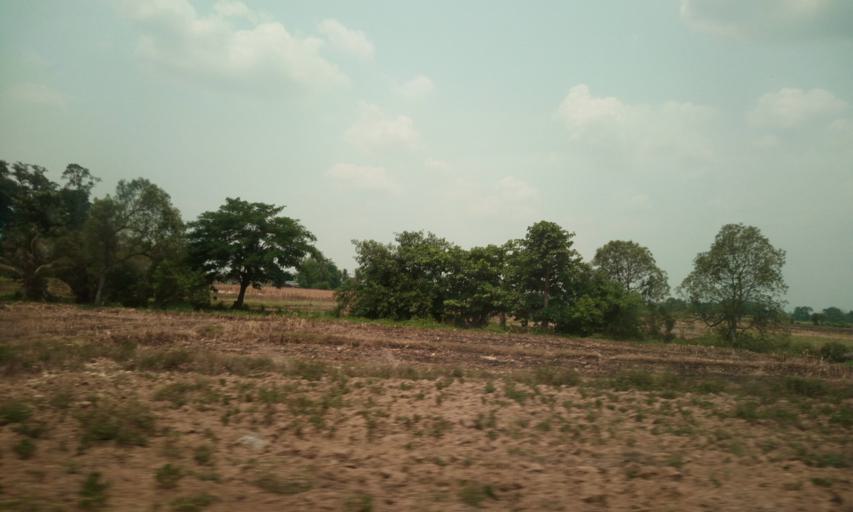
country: TH
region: Phayao
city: Phu Sang
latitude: 19.6143
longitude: 100.3215
